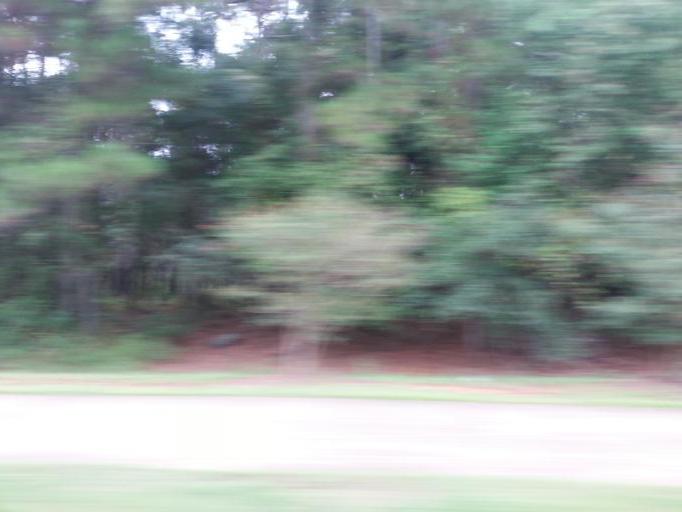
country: US
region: Alabama
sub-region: Baldwin County
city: Point Clear
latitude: 30.4377
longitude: -87.9117
